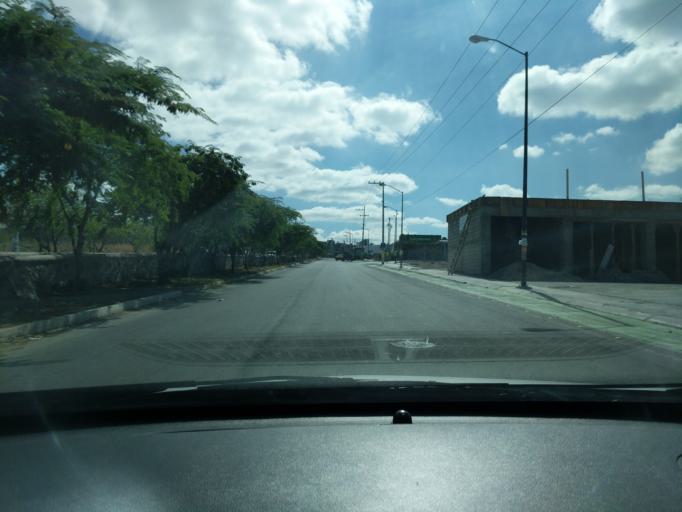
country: MX
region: Queretaro
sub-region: Queretaro
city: Patria Nueva
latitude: 20.6404
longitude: -100.4841
